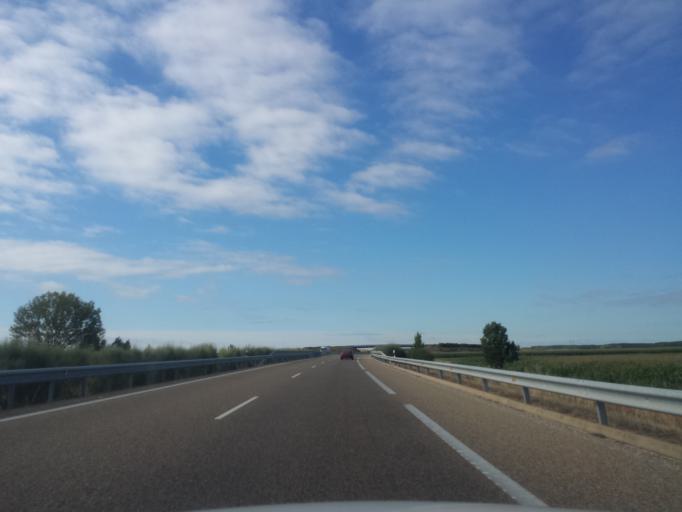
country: ES
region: Castille and Leon
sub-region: Provincia de Leon
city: Villademor de la Vega
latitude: 42.2701
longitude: -5.5902
